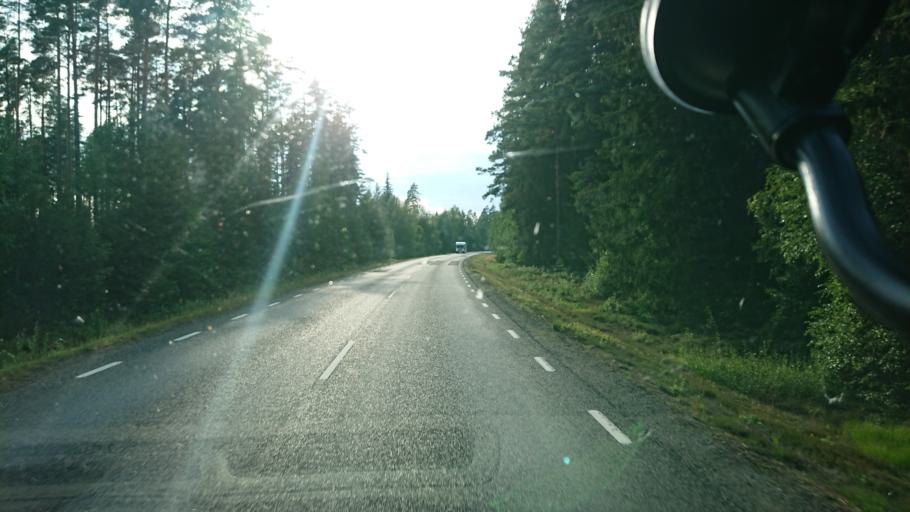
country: SE
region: Kronoberg
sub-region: Vaxjo Kommun
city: Braas
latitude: 57.0259
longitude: 14.9836
